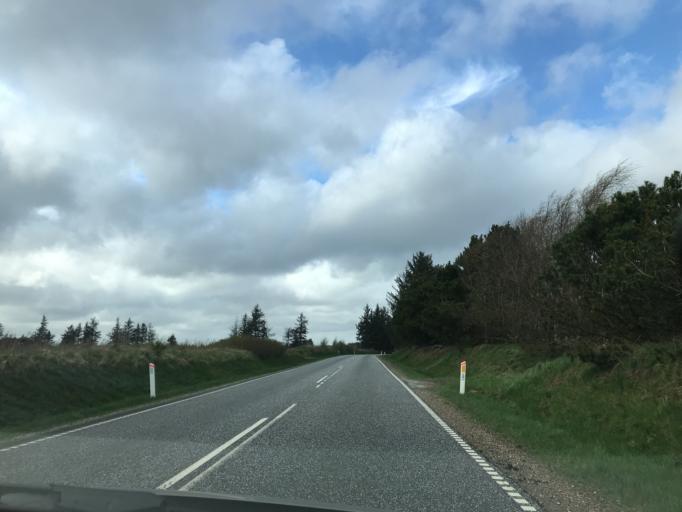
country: DK
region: Central Jutland
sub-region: Skive Kommune
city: Skive
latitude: 56.4218
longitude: 8.9711
